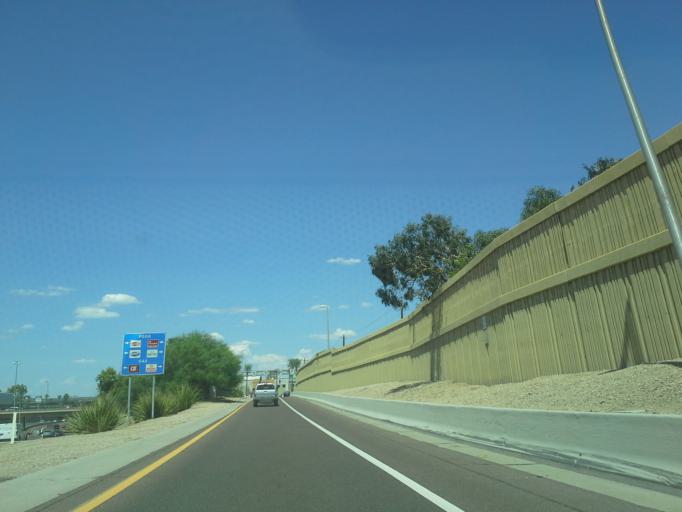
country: US
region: Arizona
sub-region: Maricopa County
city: Phoenix
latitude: 33.5034
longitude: -112.0433
